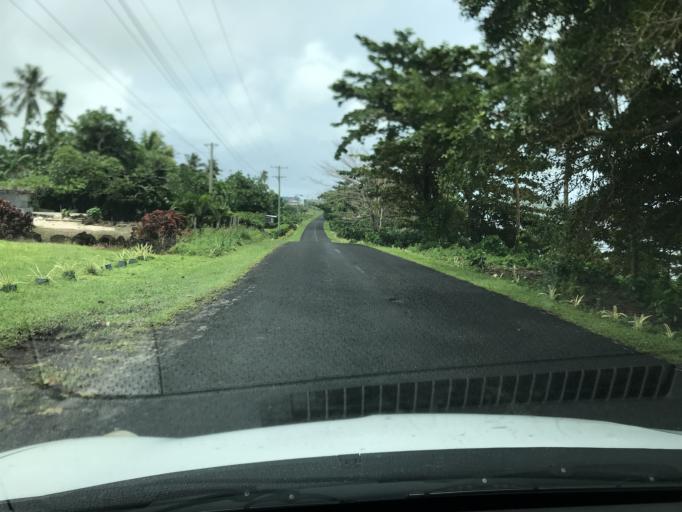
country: WS
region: Va`a-o-Fonoti
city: Samamea
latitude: -14.0441
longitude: -171.4374
